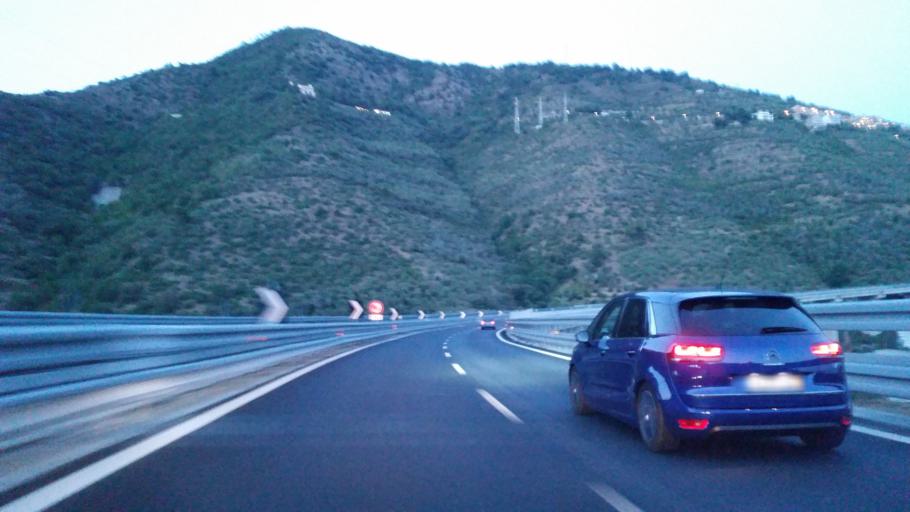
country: IT
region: Liguria
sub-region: Provincia di Imperia
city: Castellaro
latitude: 43.8700
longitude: 7.8534
